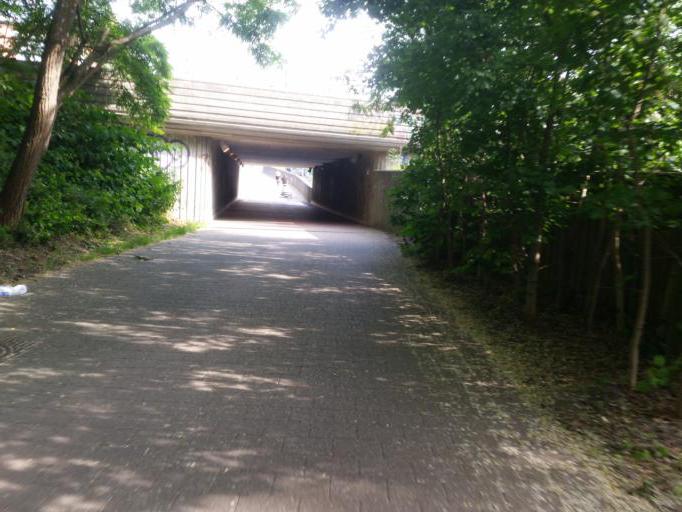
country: BE
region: Flanders
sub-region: Provincie Antwerpen
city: Mortsel
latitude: 51.1756
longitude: 4.4529
